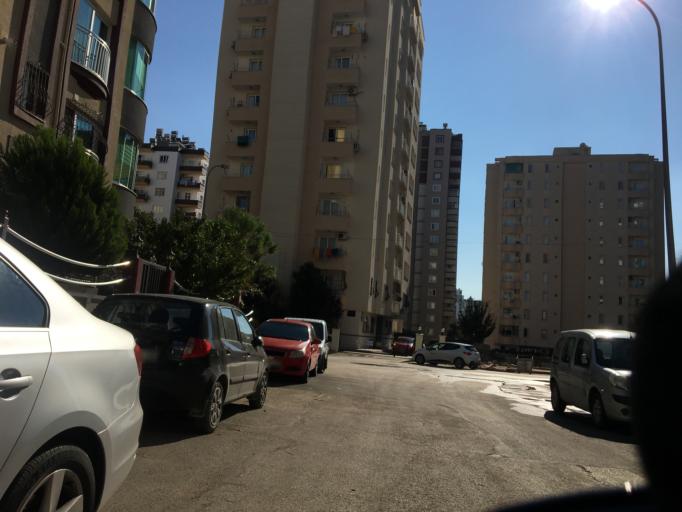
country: TR
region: Adana
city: Seyhan
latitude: 37.0270
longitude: 35.2851
